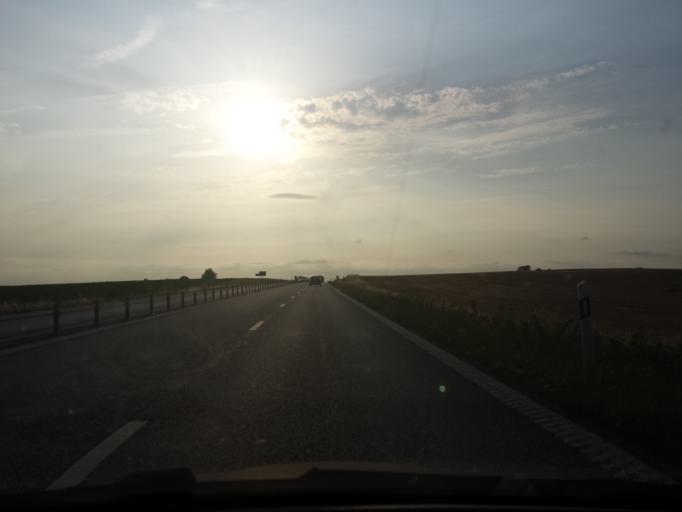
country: SE
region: Skane
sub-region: Skurups Kommun
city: Rydsgard
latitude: 55.4765
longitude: 13.6442
